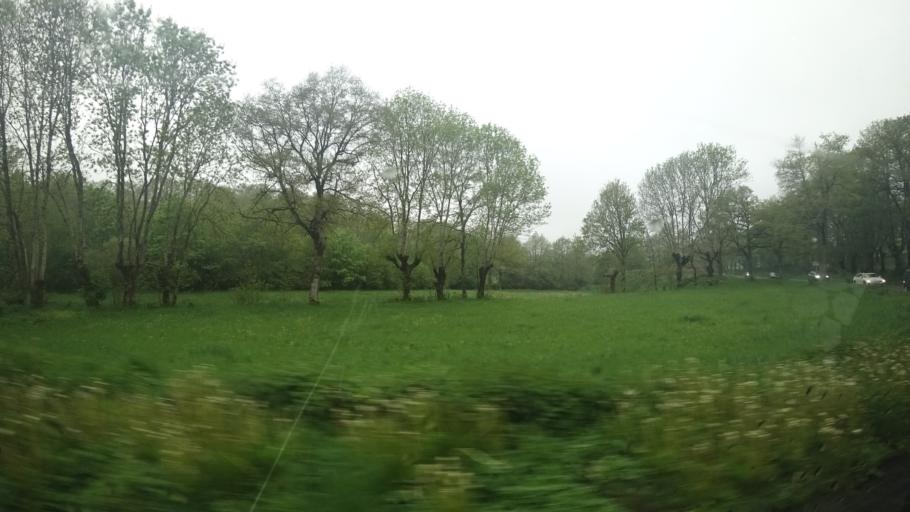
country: FR
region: Midi-Pyrenees
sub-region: Departement de l'Aveyron
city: Laissac
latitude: 44.2970
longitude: 2.8363
